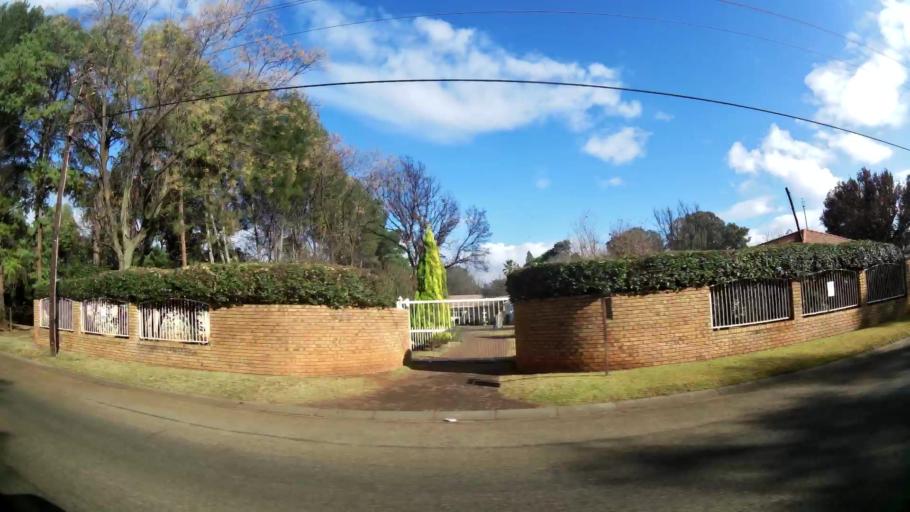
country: ZA
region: Gauteng
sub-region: Sedibeng District Municipality
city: Meyerton
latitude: -26.5318
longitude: 28.0634
